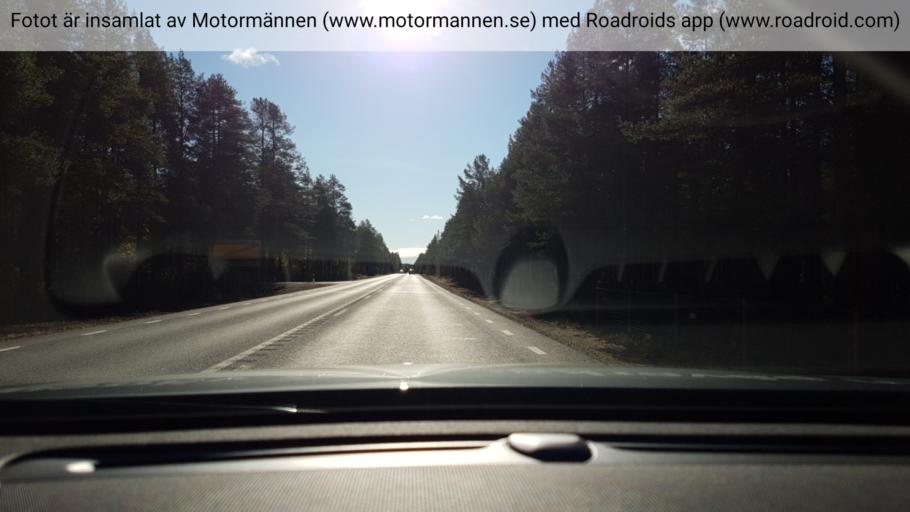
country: SE
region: Vaesterbotten
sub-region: Skelleftea Kommun
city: Burea
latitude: 64.5666
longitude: 21.2287
